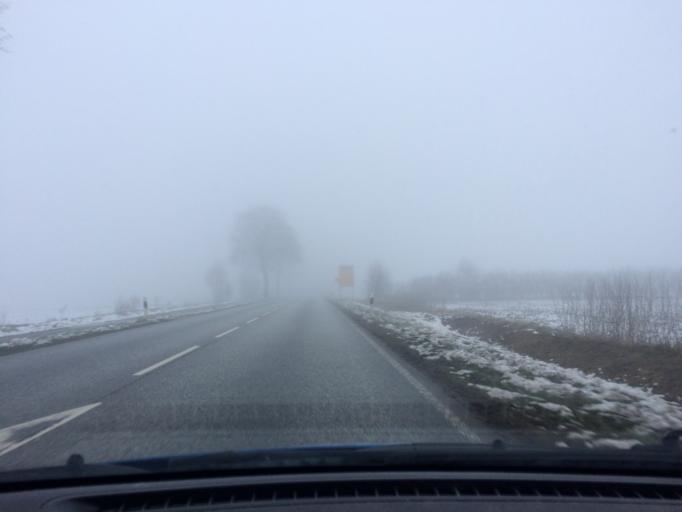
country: DE
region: Schleswig-Holstein
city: Grabau
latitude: 53.5188
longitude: 10.5006
